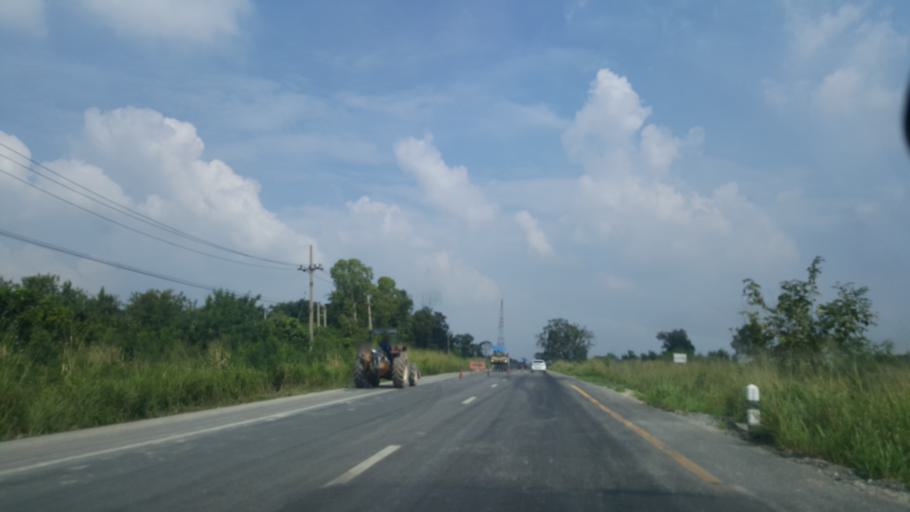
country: TH
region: Rayong
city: Ban Chang
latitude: 12.8635
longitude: 101.0241
